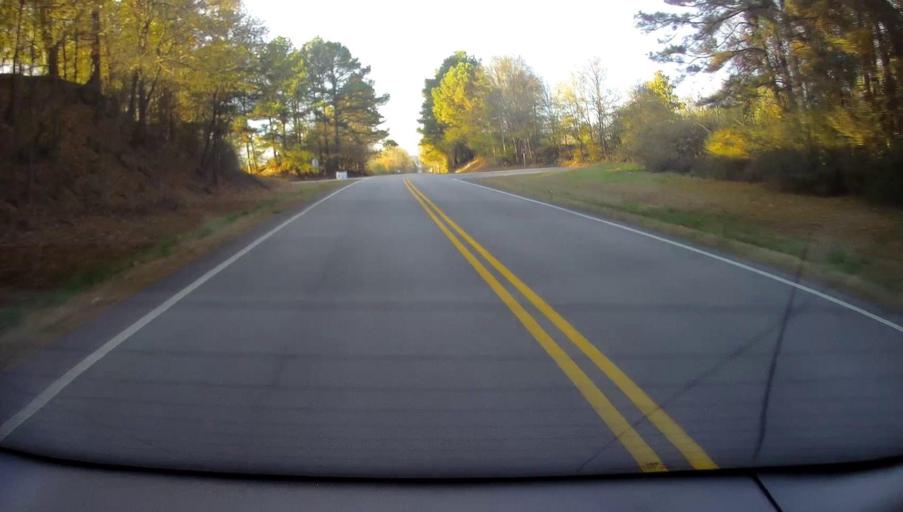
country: US
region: Alabama
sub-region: Blount County
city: Blountsville
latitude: 34.1837
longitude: -86.5234
